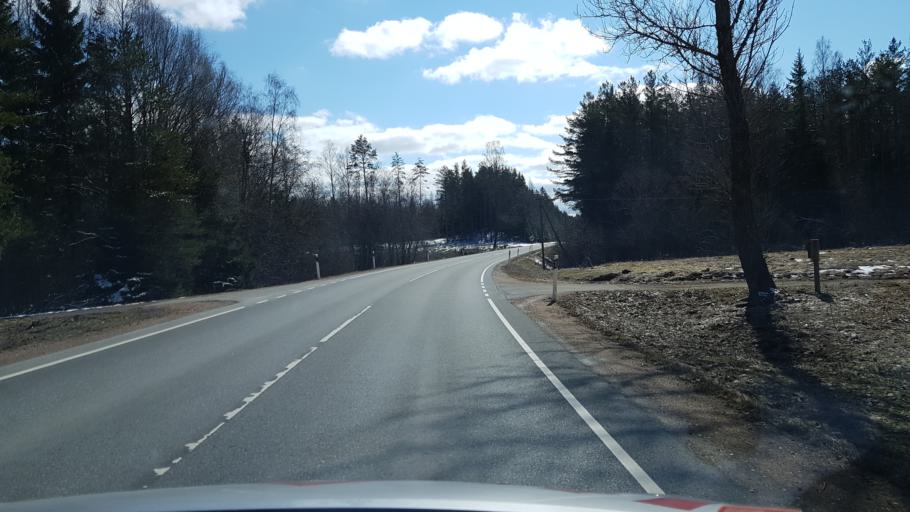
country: EE
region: Laeaene-Virumaa
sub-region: Kadrina vald
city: Kadrina
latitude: 59.3998
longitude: 26.0126
